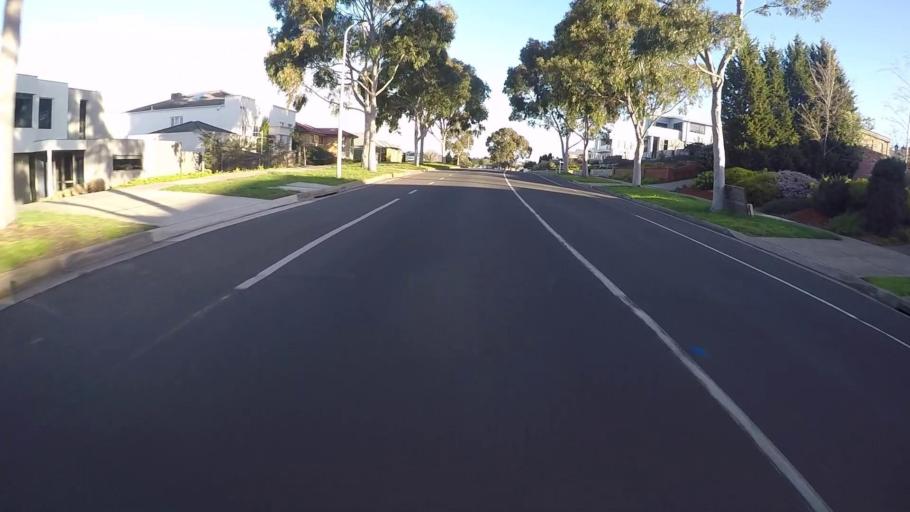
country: AU
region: Victoria
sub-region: Greater Geelong
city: Wandana Heights
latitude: -38.1670
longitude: 144.3021
